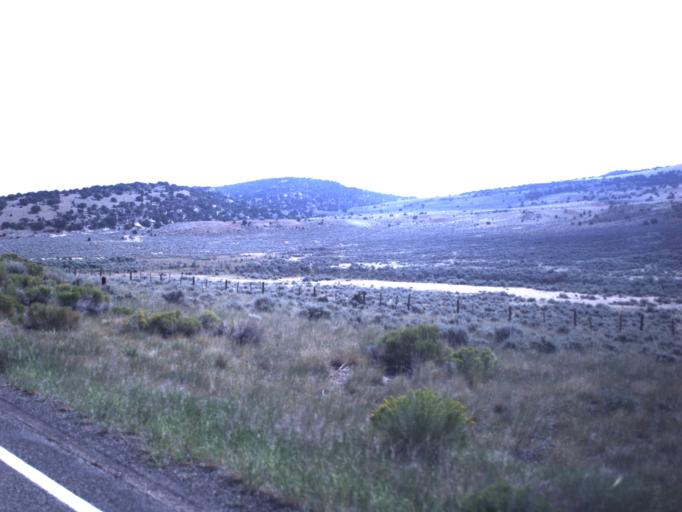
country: US
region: Utah
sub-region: Daggett County
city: Manila
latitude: 40.9332
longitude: -109.7028
